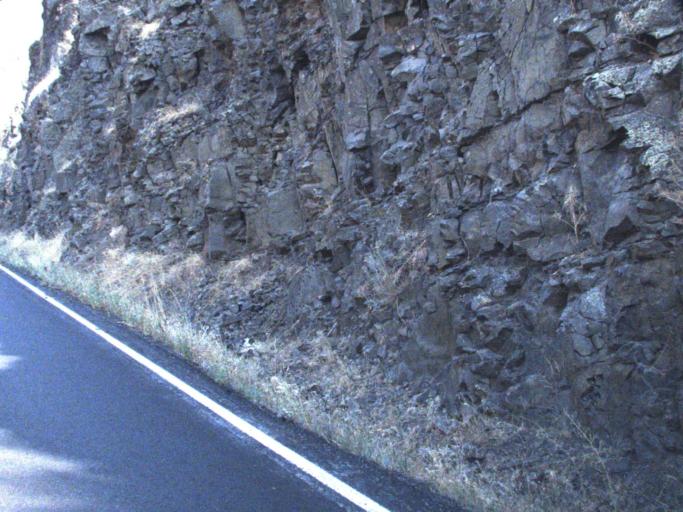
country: US
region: Washington
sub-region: Yakima County
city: Selah
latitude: 46.7668
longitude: -120.4535
